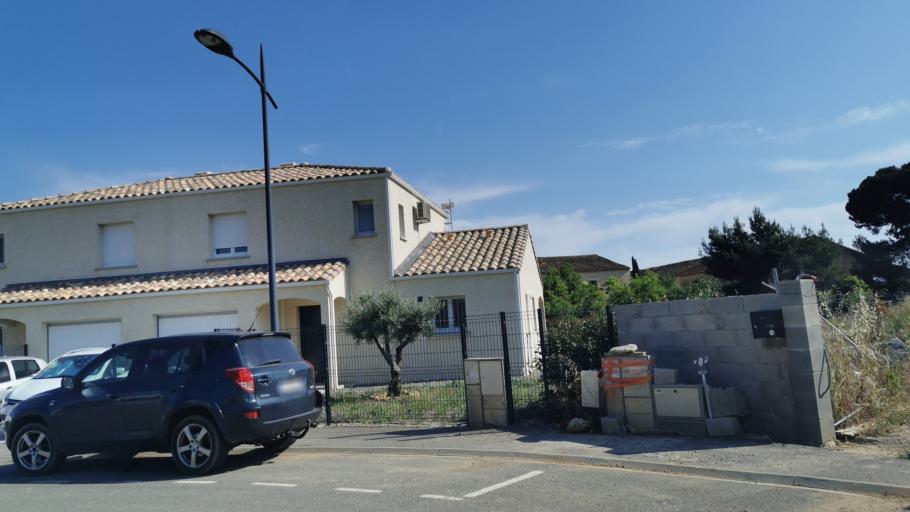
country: FR
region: Languedoc-Roussillon
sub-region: Departement de l'Aude
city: Peyriac-de-Mer
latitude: 43.1343
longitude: 2.9580
